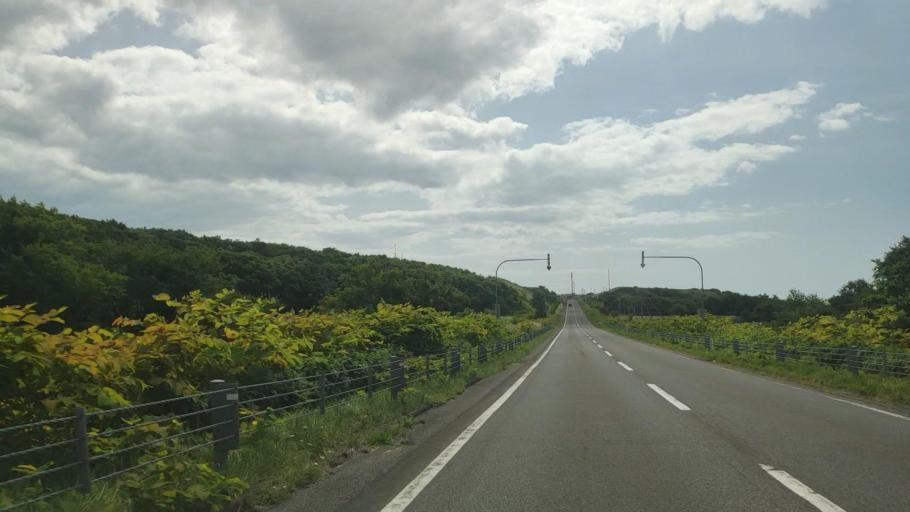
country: JP
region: Hokkaido
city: Rumoi
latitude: 44.6064
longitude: 141.7970
